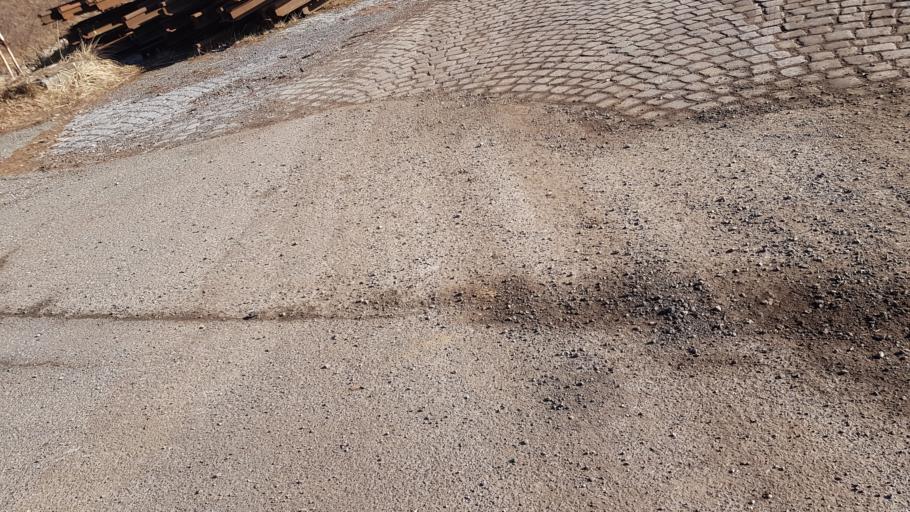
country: CZ
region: Olomoucky
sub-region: Okres Jesenik
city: Jesenik
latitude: 50.2269
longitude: 17.1900
